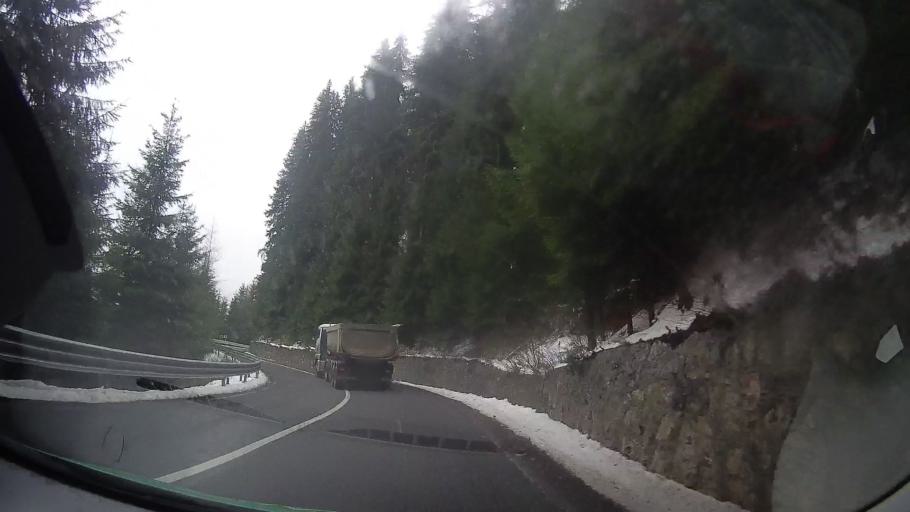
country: RO
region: Neamt
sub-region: Comuna Bicaz Chei
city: Bicaz Chei
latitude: 46.7814
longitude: 25.7485
